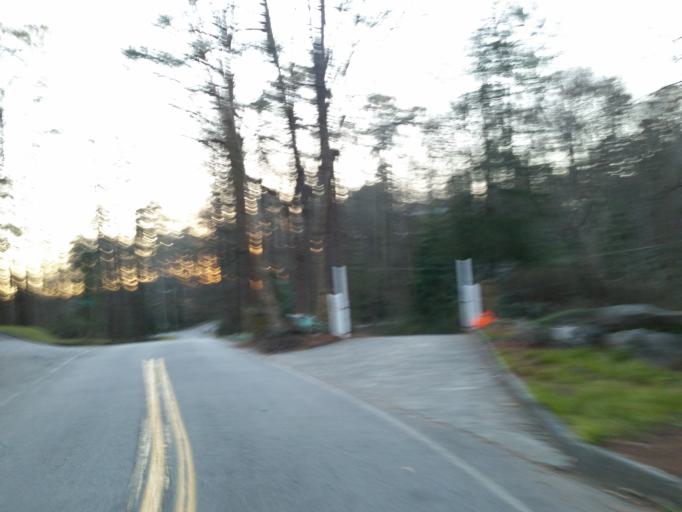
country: US
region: Georgia
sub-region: Cobb County
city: Vinings
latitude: 33.8401
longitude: -84.4527
